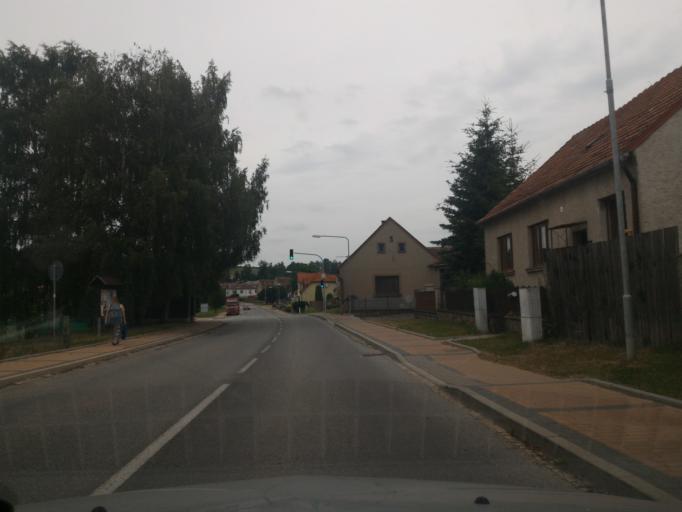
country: CZ
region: Vysocina
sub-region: Okres Jihlava
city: Telc
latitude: 49.1812
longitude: 15.4140
